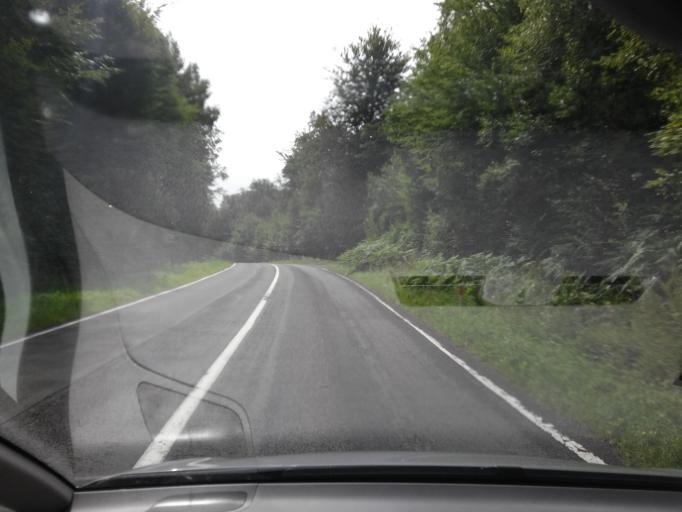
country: BE
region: Wallonia
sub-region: Province du Luxembourg
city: Chiny
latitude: 49.7764
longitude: 5.3502
